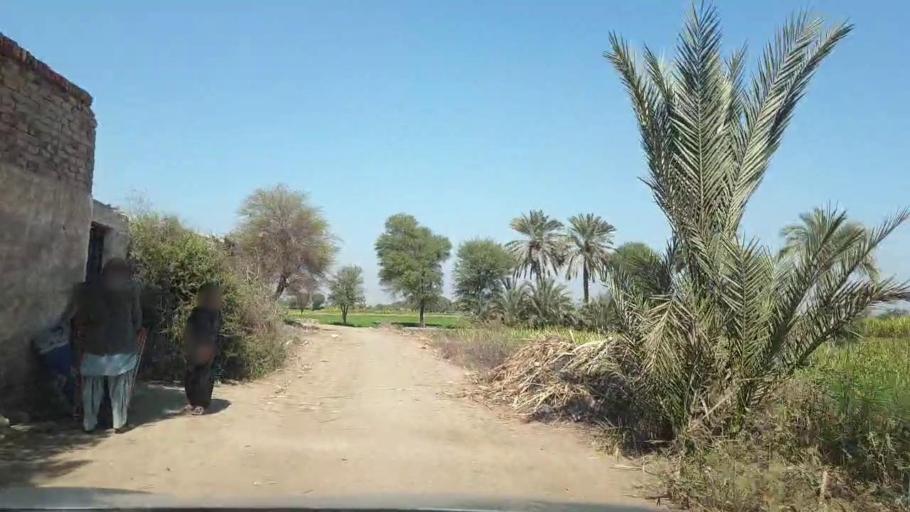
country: PK
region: Sindh
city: Tando Adam
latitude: 25.6307
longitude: 68.6806
